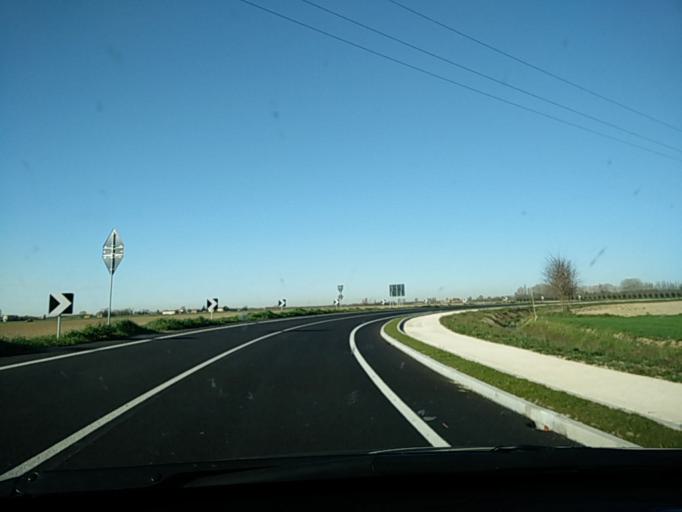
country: IT
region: Veneto
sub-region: Provincia di Venezia
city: Quarto d'Altino
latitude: 45.5667
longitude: 12.3916
